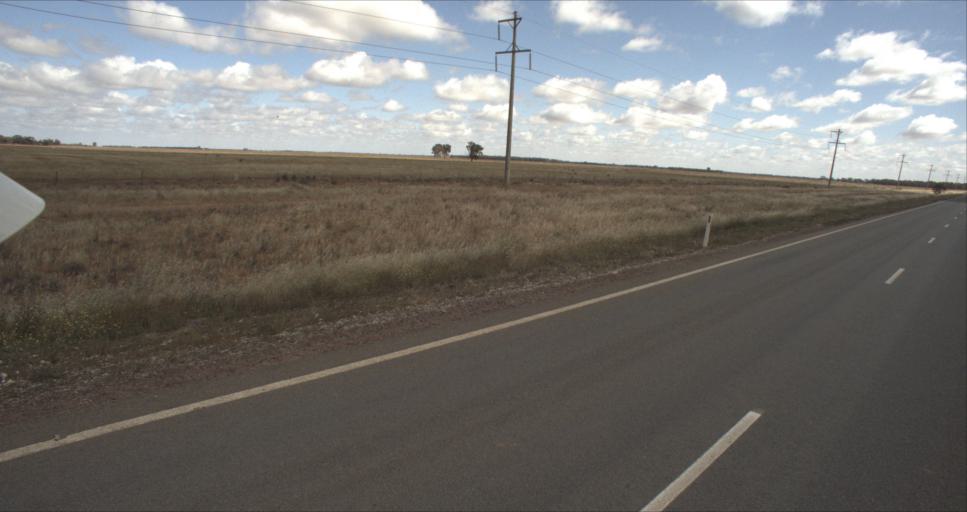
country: AU
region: New South Wales
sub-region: Murrumbidgee Shire
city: Darlington Point
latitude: -34.5912
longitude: 146.1635
